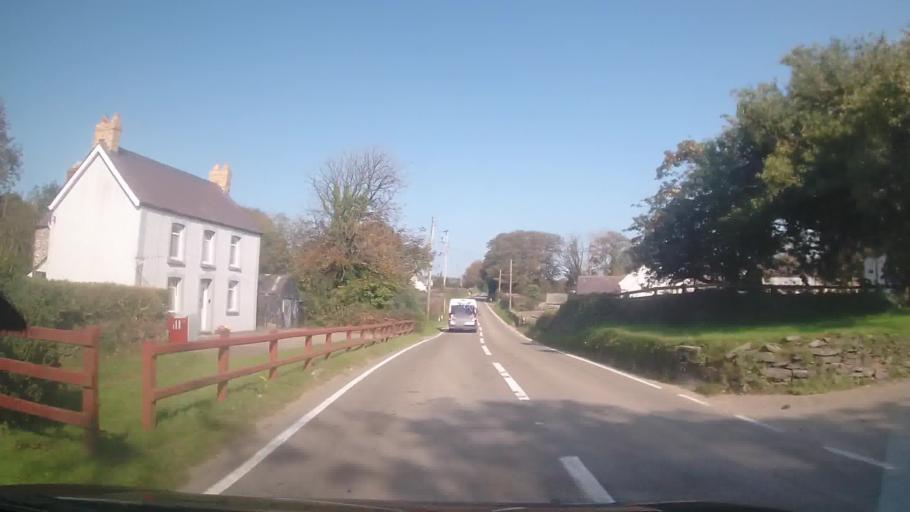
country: GB
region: Wales
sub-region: Pembrokeshire
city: Crymych
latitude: 52.0093
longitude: -4.7193
